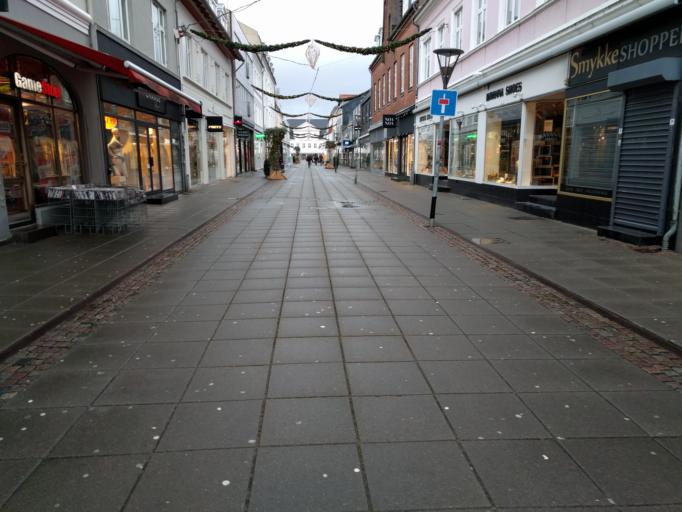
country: DK
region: Central Jutland
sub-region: Silkeborg Kommune
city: Silkeborg
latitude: 56.1680
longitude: 9.5502
